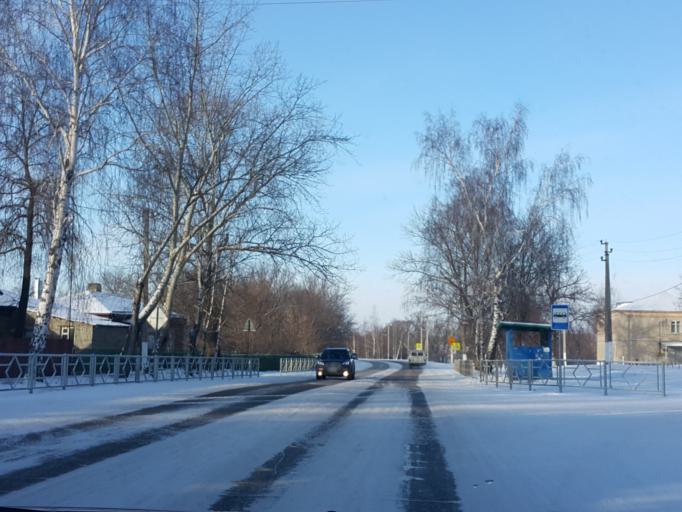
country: RU
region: Tambov
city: Znamenka
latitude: 52.4164
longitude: 41.4393
